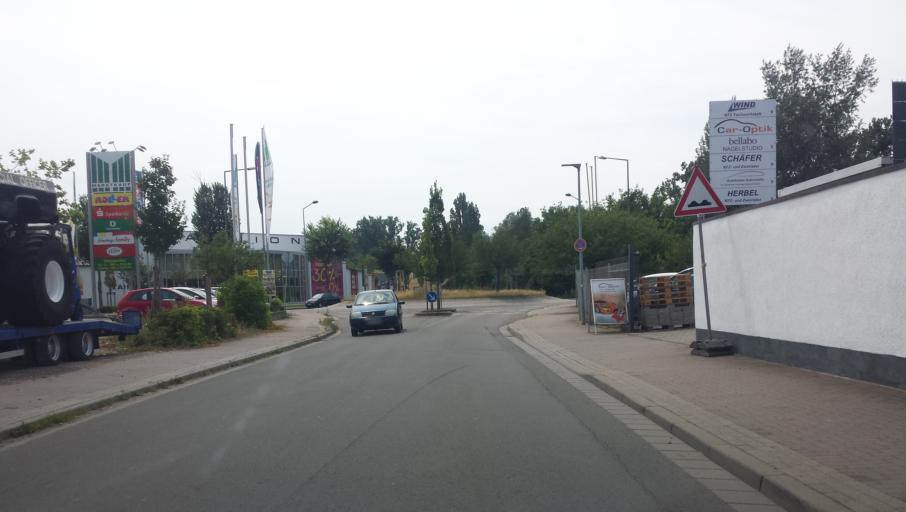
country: DE
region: Rheinland-Pfalz
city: Speyer
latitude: 49.3336
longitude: 8.4429
